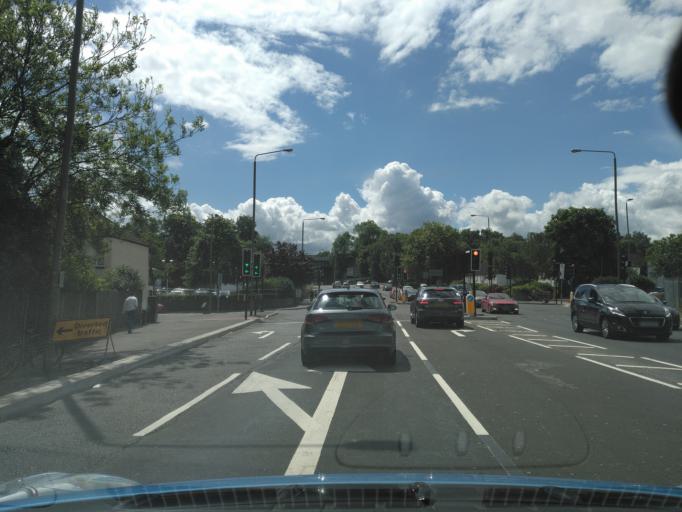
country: GB
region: England
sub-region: Greater London
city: Orpington
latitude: 51.3968
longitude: 0.1127
